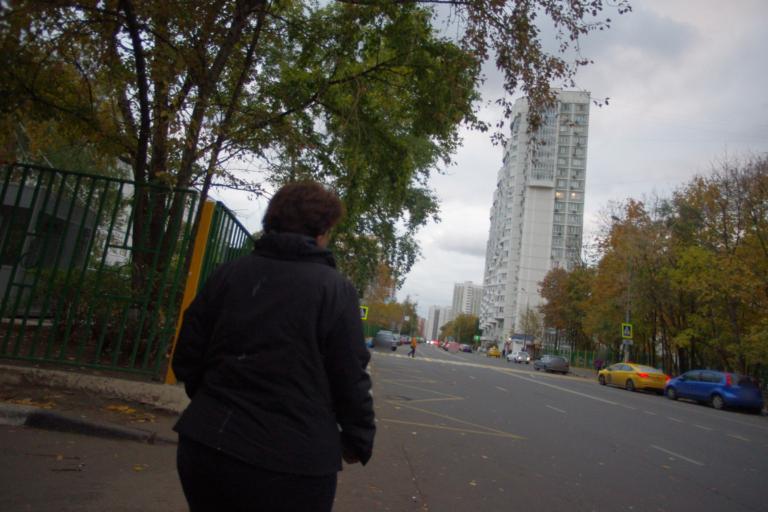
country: RU
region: Moskovskaya
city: Semenovskoye
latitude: 55.6629
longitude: 37.5257
